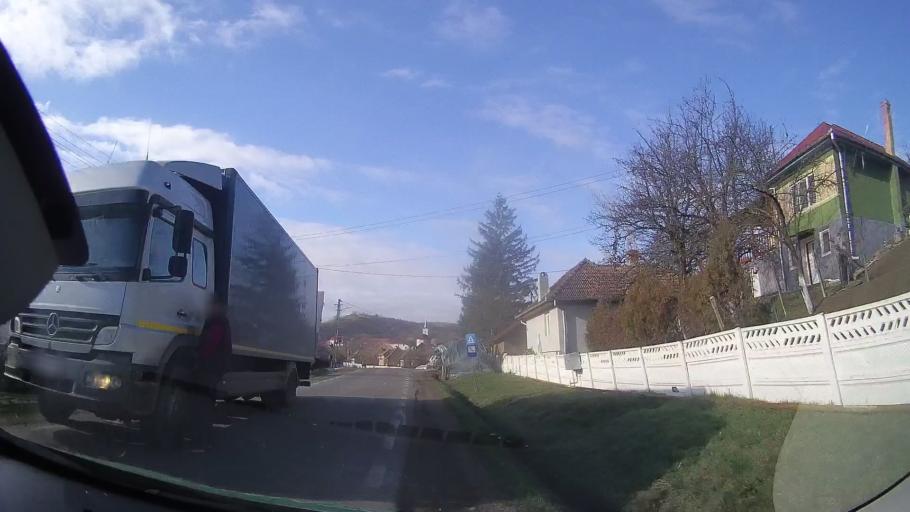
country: RO
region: Mures
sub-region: Comuna Papiu Ilarian
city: Papiu Ilarian
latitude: 46.5602
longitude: 24.2010
